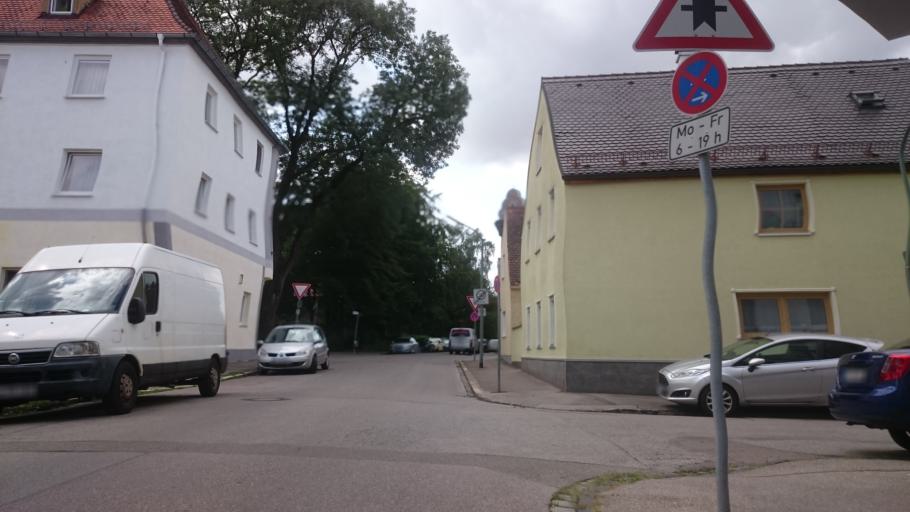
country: DE
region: Bavaria
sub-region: Swabia
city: Augsburg
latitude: 48.3757
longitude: 10.9242
